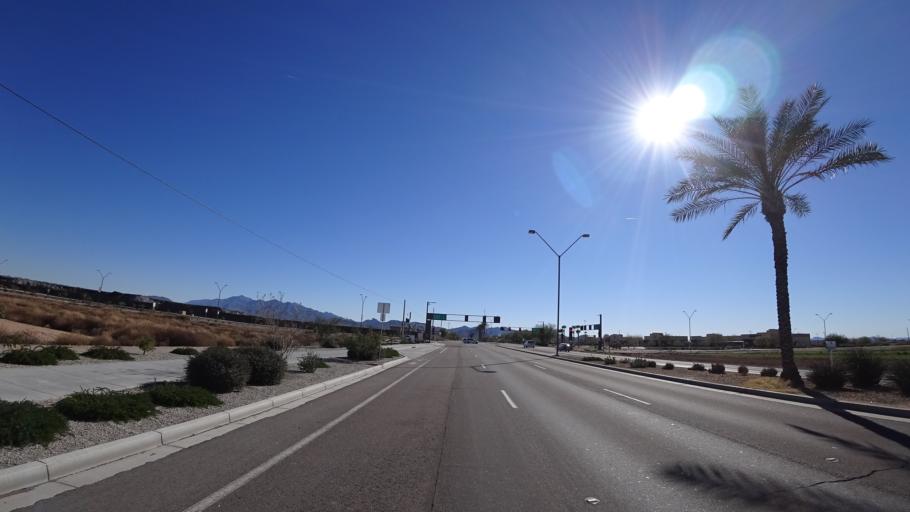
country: US
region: Arizona
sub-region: Maricopa County
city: Goodyear
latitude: 33.4145
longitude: -112.3922
